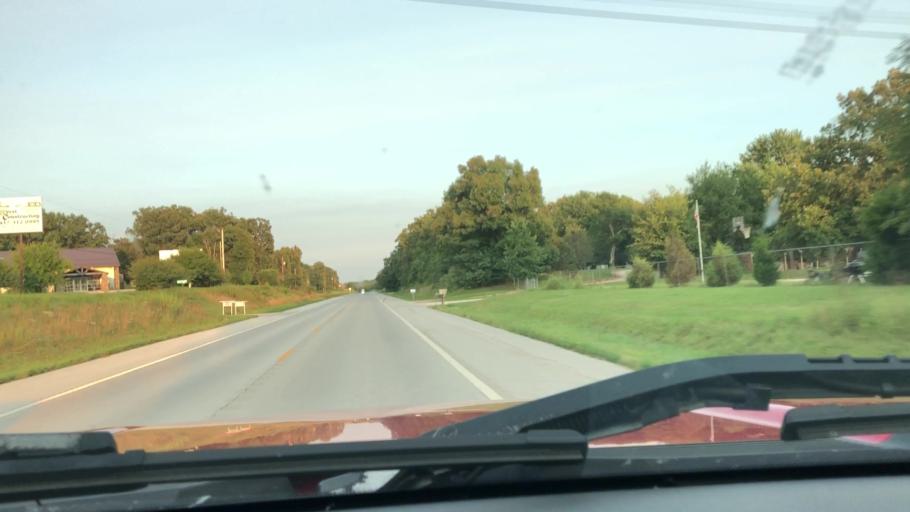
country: US
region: Missouri
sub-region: Jasper County
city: Duquesne
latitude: 36.9736
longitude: -94.4552
